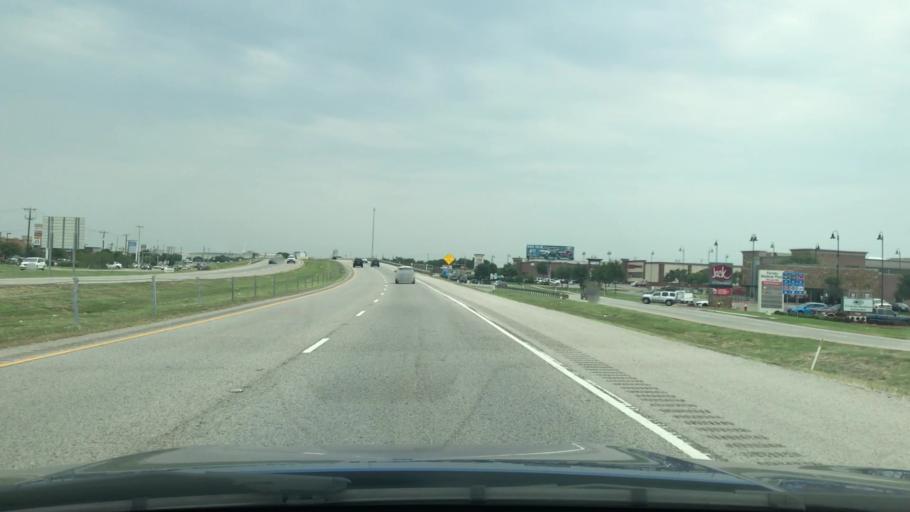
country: US
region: Texas
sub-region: Kaufman County
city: Forney
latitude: 32.7444
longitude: -96.4519
